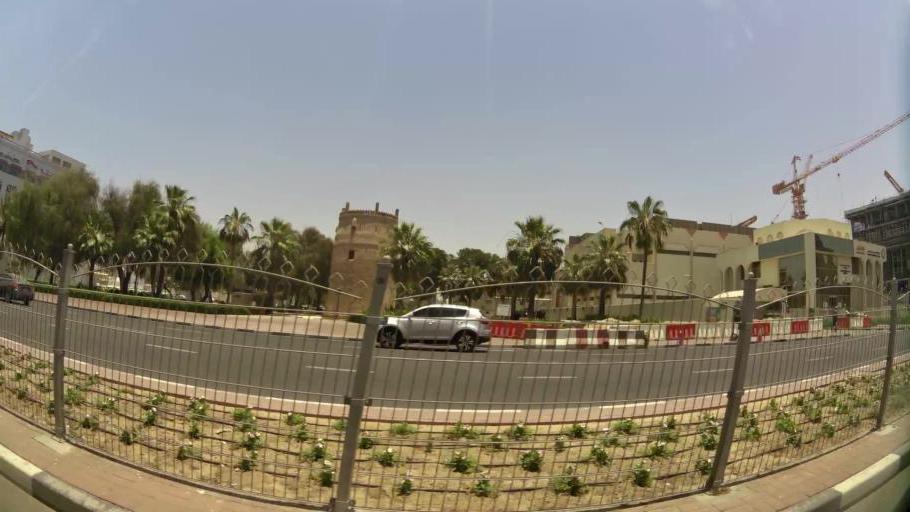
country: AE
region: Ash Shariqah
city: Sharjah
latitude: 25.2750
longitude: 55.3156
